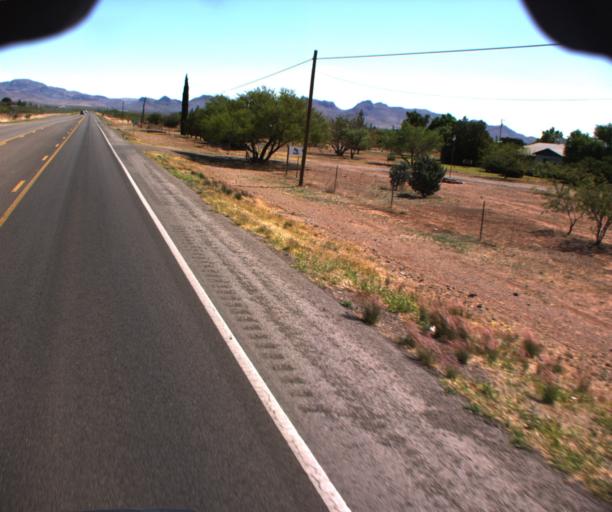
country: US
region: Arizona
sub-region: Cochise County
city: Douglas
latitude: 31.3675
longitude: -109.5361
